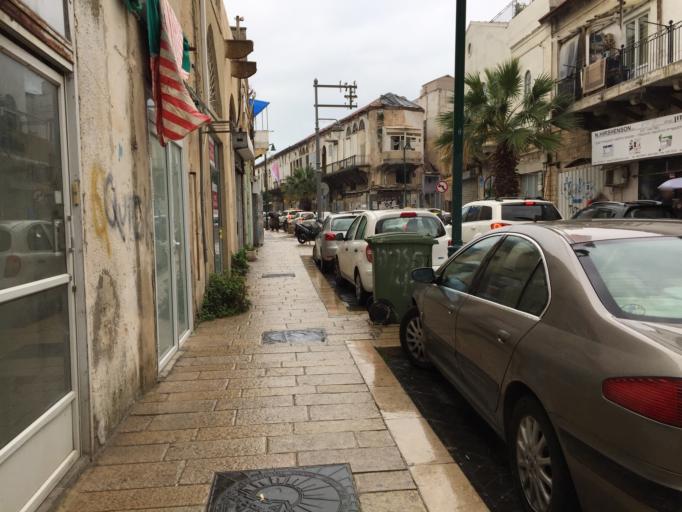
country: IL
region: Tel Aviv
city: Yafo
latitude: 32.0563
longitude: 34.7580
